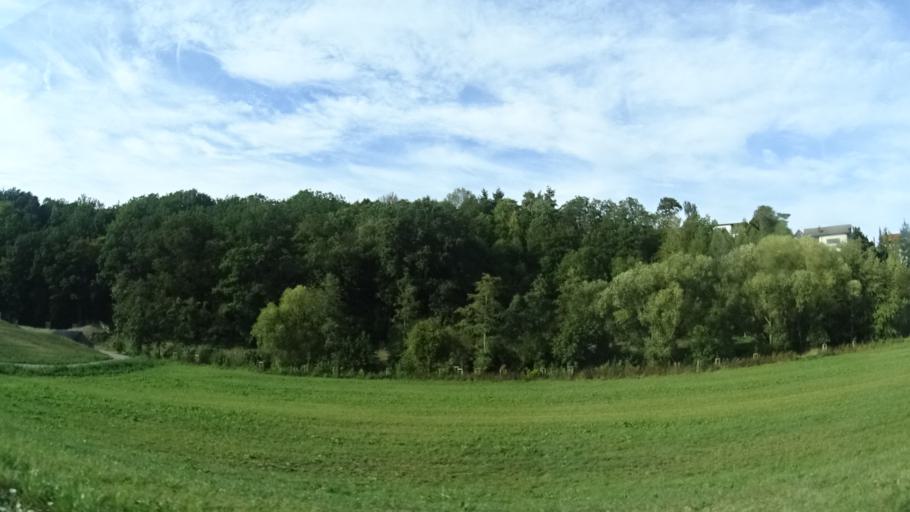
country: DE
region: Hesse
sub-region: Regierungsbezirk Kassel
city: Kunzell
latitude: 50.5199
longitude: 9.7258
